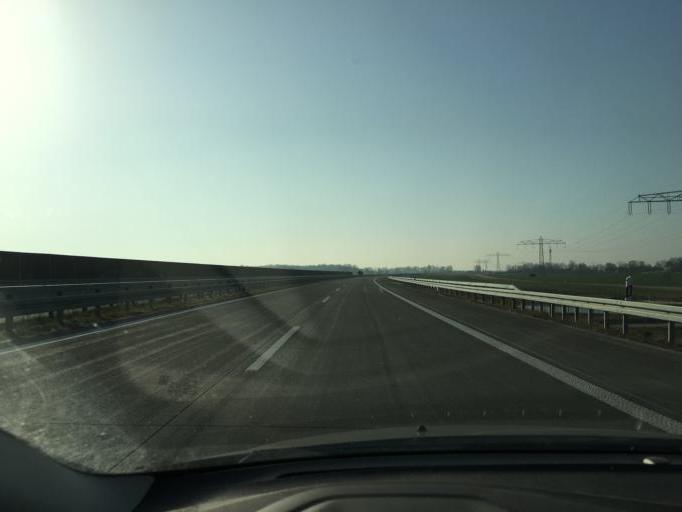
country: DE
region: Saxony
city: Frohburg
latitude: 51.0688
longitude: 12.6131
